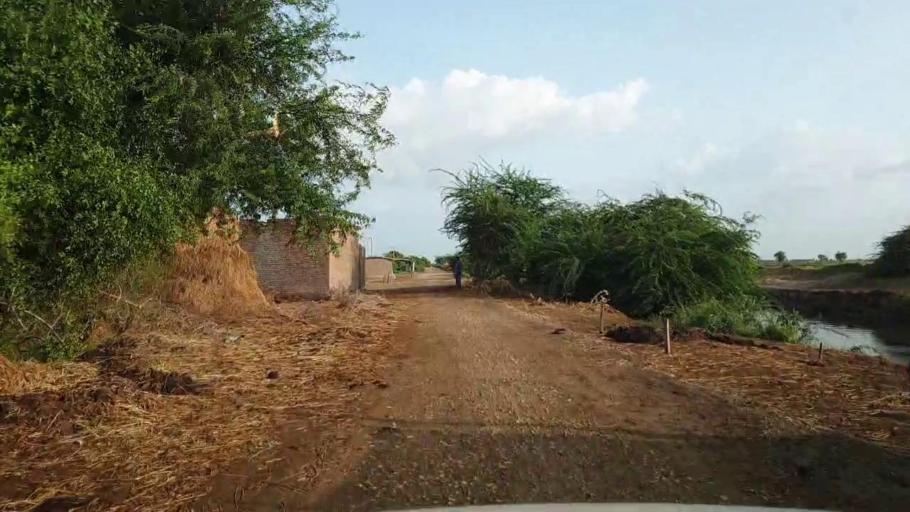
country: PK
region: Sindh
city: Kario
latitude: 24.8202
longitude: 68.6465
